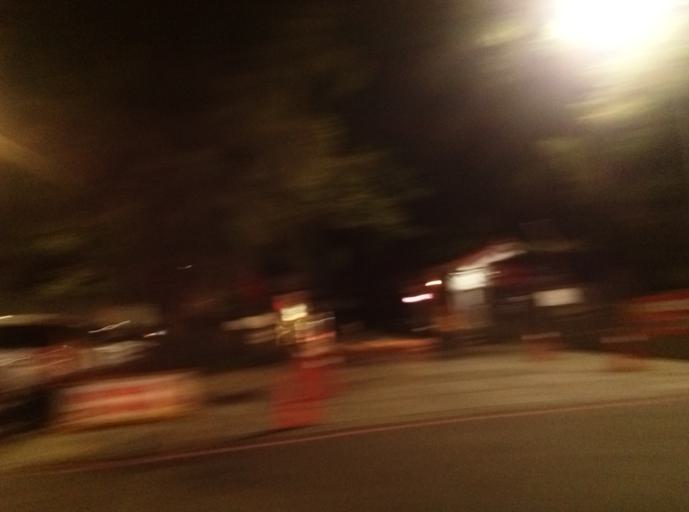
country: TW
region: Taiwan
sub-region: Hsinchu
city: Hsinchu
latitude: 24.7947
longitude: 120.9763
